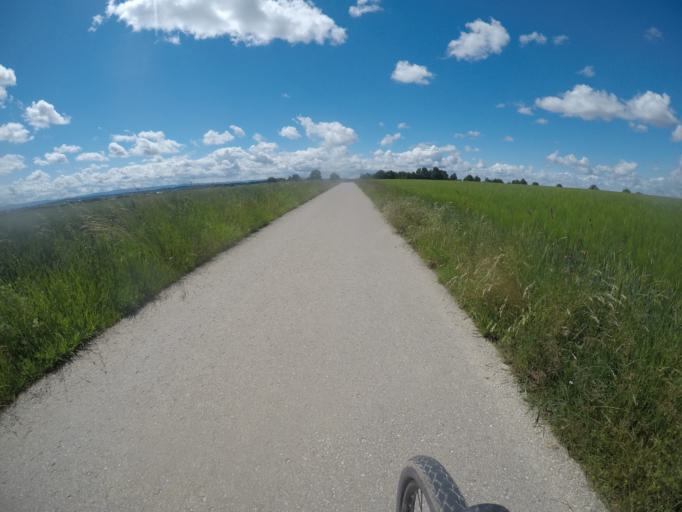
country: DE
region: Baden-Wuerttemberg
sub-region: Regierungsbezirk Stuttgart
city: Motzingen
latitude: 48.4880
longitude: 8.7498
